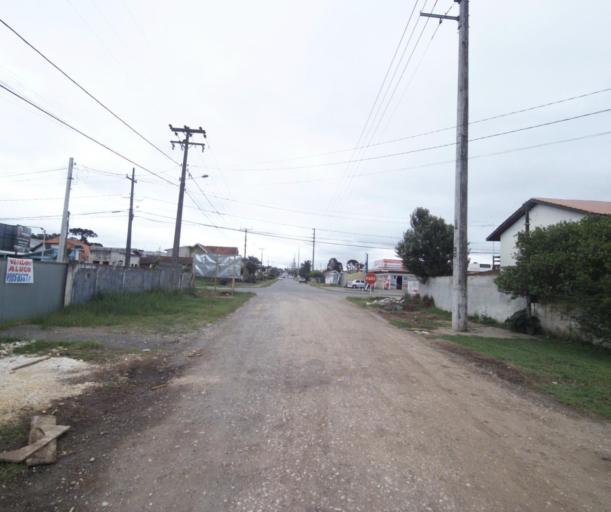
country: BR
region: Parana
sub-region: Quatro Barras
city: Quatro Barras
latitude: -25.3641
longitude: -49.0958
